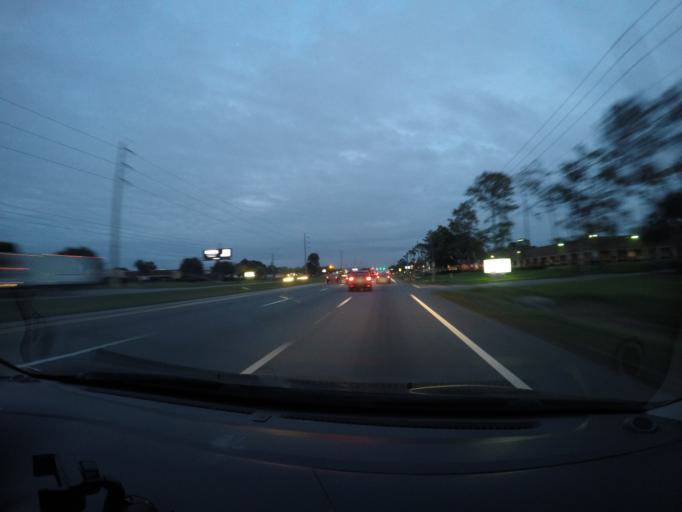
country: US
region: Florida
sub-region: Orange County
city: Oak Ridge
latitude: 28.4503
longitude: -81.4153
